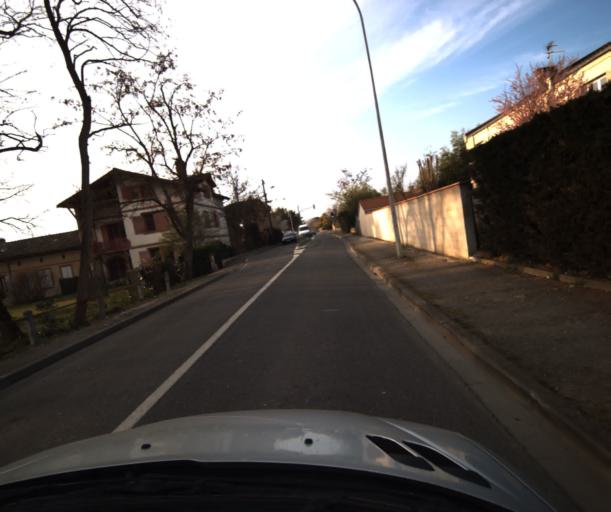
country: FR
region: Midi-Pyrenees
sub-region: Departement de la Haute-Garonne
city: Fonbeauzard
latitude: 43.6859
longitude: 1.4390
